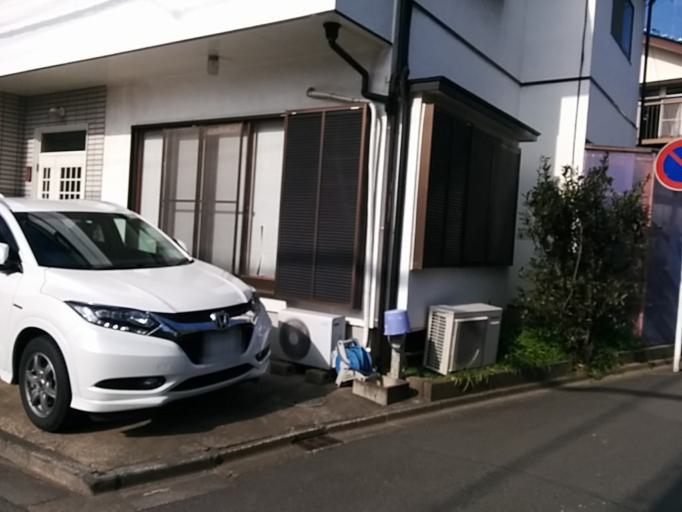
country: JP
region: Saitama
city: Kawagoe
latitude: 35.9227
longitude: 139.4920
